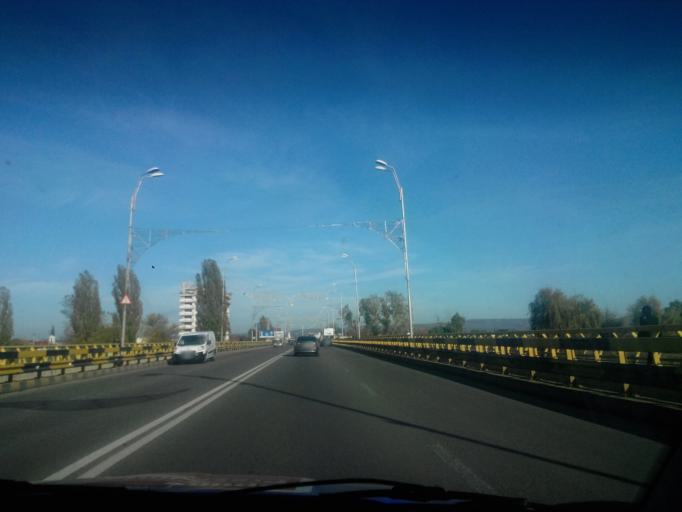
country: RO
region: Bacau
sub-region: Municipiul Bacau
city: Bacau
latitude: 46.5725
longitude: 26.9242
